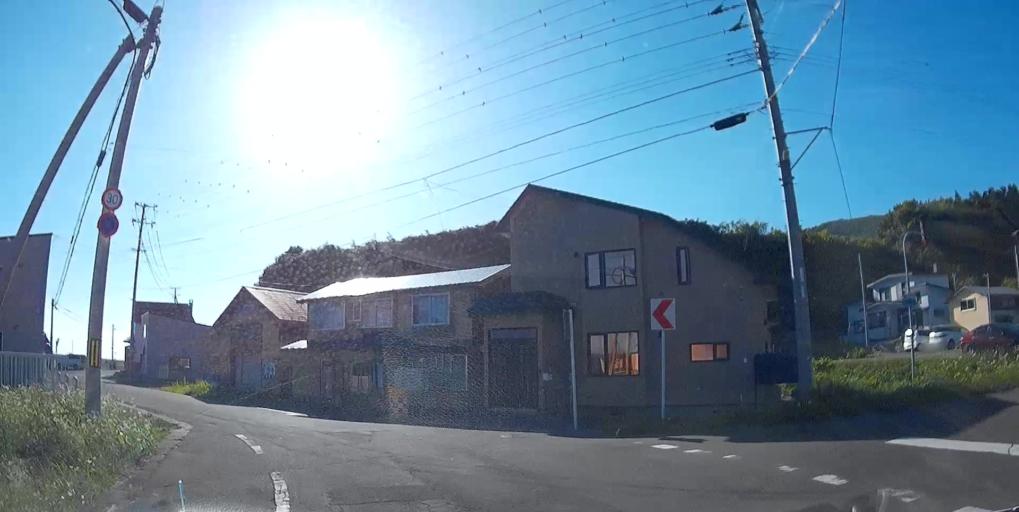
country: JP
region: Hokkaido
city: Kamiiso
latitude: 42.2300
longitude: 139.8114
